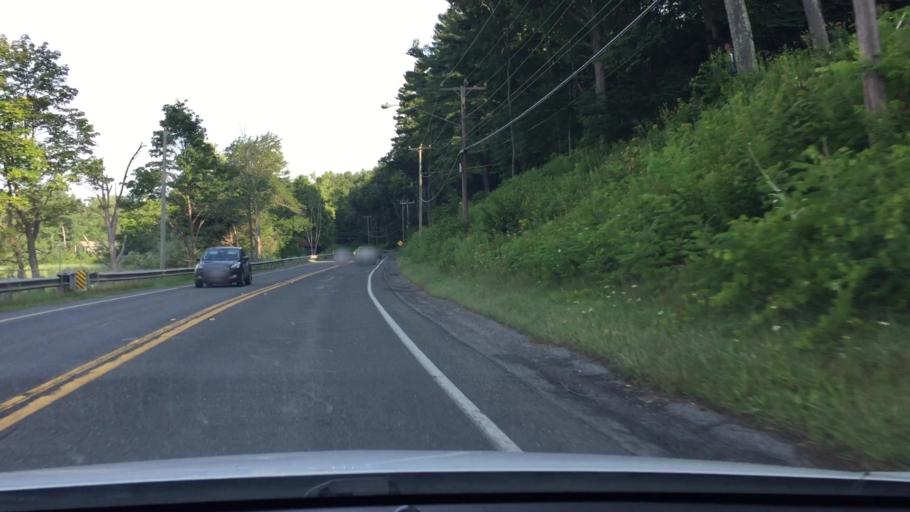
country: US
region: Massachusetts
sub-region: Berkshire County
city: Becket
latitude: 42.2883
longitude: -73.1523
